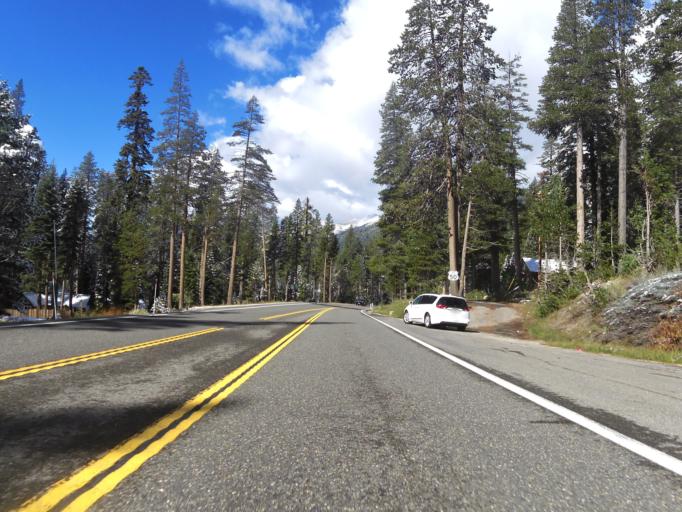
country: US
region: California
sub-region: El Dorado County
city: South Lake Tahoe
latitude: 38.8244
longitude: -120.0446
